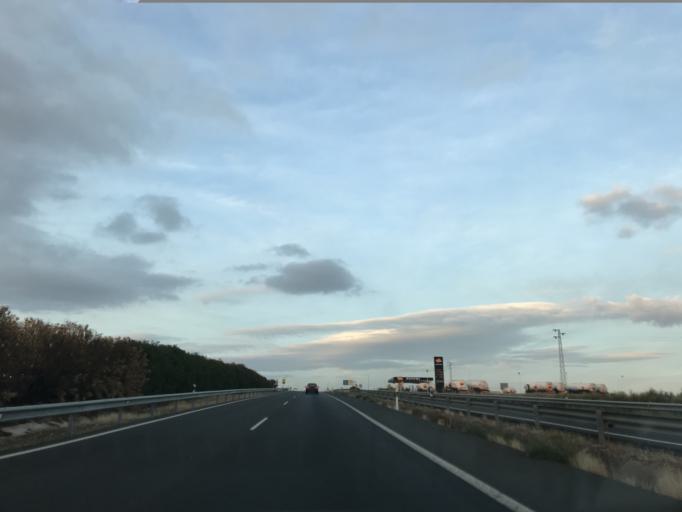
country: ES
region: Andalusia
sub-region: Province of Cordoba
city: La Victoria
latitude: 37.7568
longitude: -4.8299
